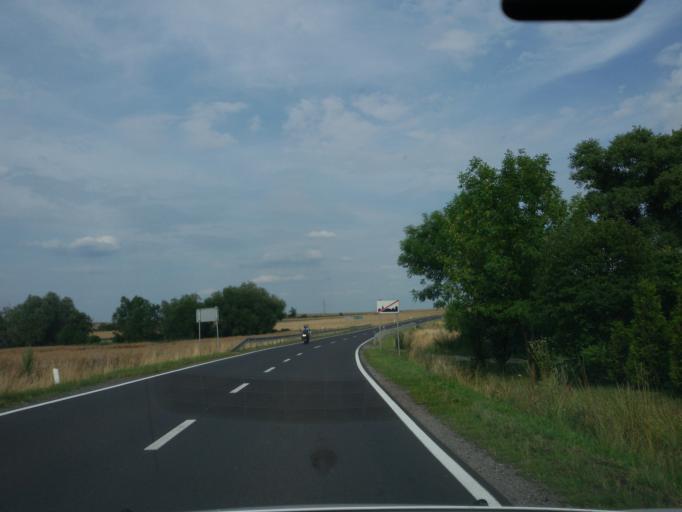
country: PL
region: Lower Silesian Voivodeship
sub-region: Powiat polkowicki
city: Radwanice
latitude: 51.6309
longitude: 15.9661
